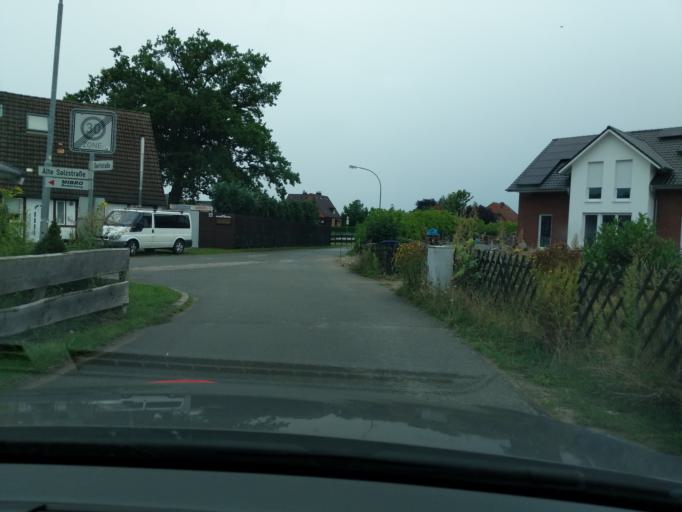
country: DE
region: Schleswig-Holstein
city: Schnakenbek
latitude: 53.3861
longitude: 10.5010
